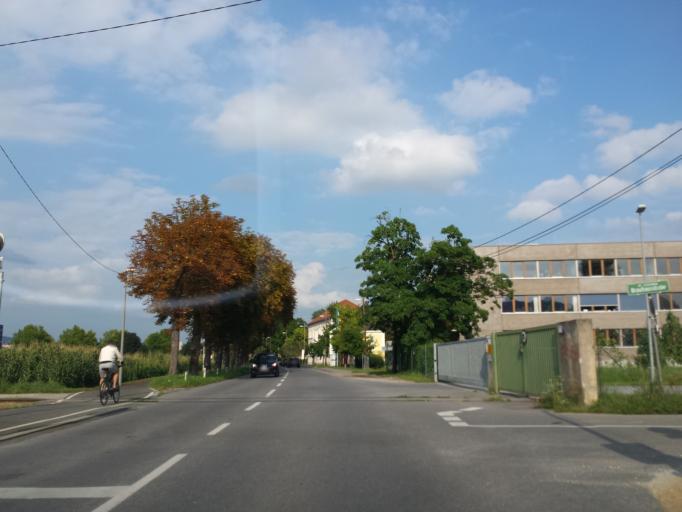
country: AT
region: Styria
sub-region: Graz Stadt
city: Wetzelsdorf
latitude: 47.0648
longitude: 15.4068
